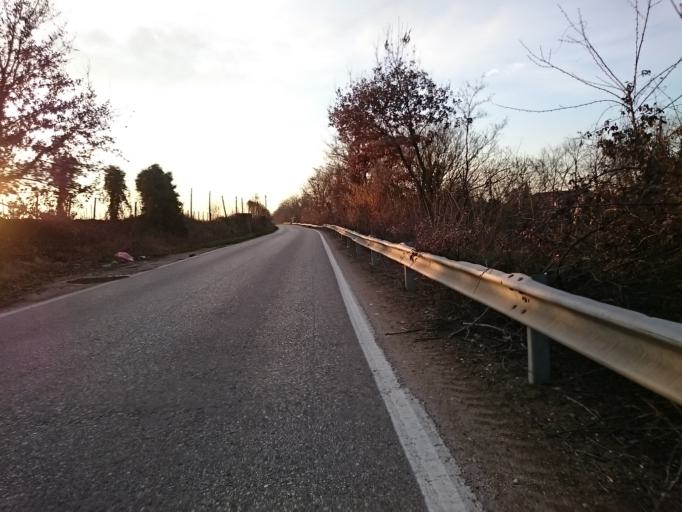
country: IT
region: Veneto
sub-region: Provincia di Verona
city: Castelnuovo del Garda
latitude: 45.4284
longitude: 10.7712
